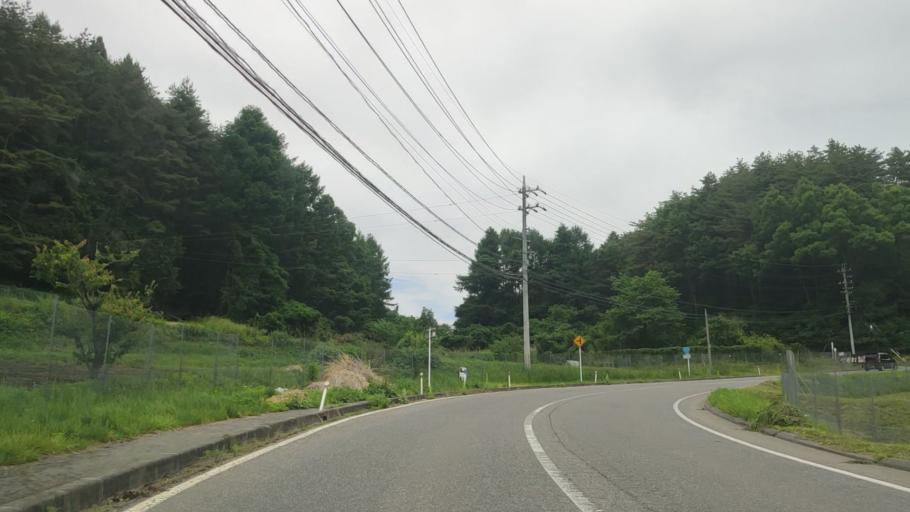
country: JP
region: Nagano
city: Kamimaruko
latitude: 36.2772
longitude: 138.2813
